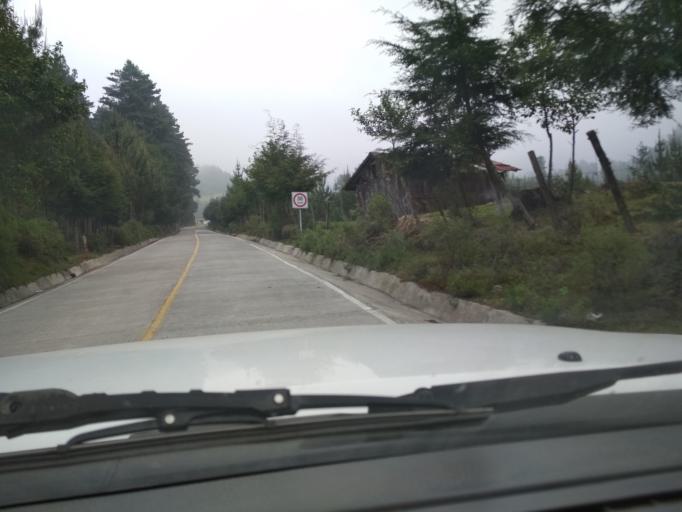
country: MX
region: Veracruz
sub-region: La Perla
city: Chilapa
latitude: 18.9943
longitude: -97.1856
